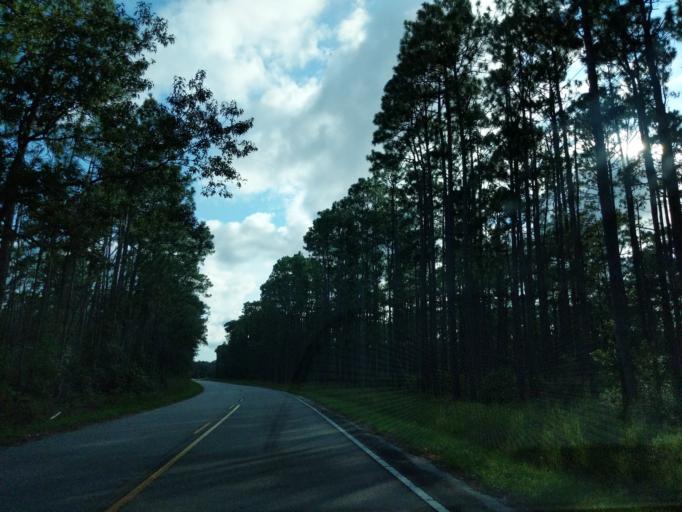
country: US
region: South Carolina
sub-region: Charleston County
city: Awendaw
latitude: 33.1326
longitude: -79.4426
